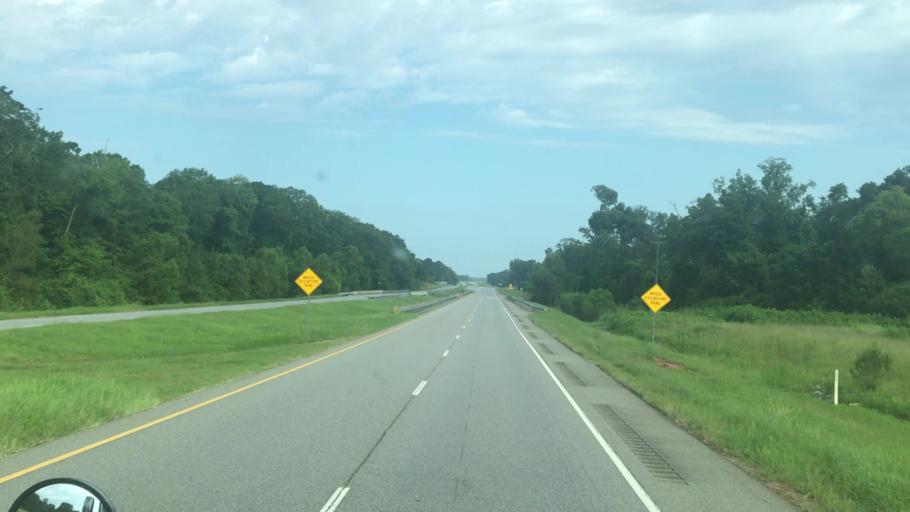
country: US
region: Georgia
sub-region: Early County
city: Blakely
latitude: 31.3317
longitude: -84.8948
